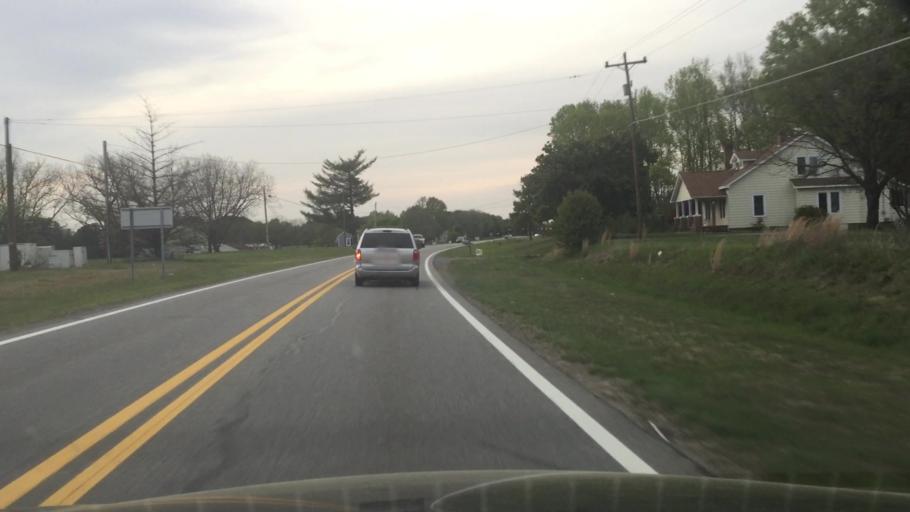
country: US
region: North Carolina
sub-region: Rockingham County
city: Reidsville
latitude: 36.3078
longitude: -79.6263
